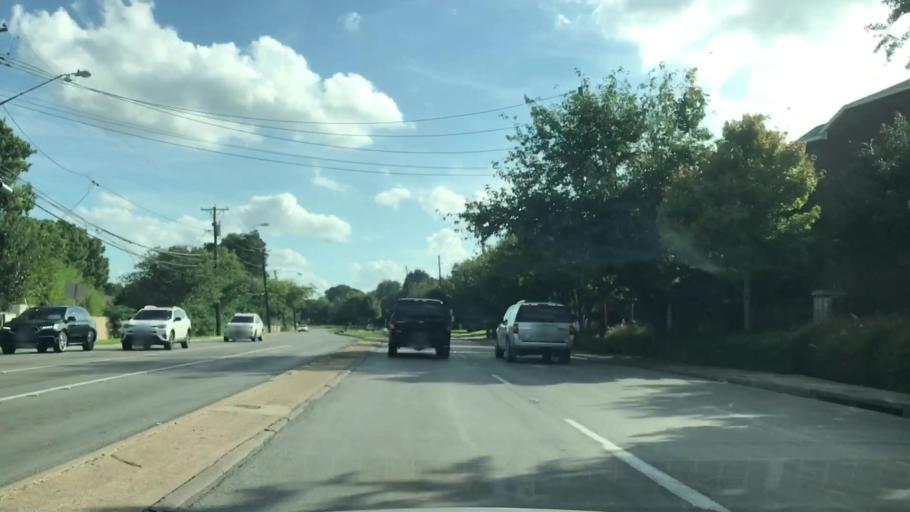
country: US
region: Texas
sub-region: Dallas County
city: Highland Park
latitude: 32.8508
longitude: -96.7607
